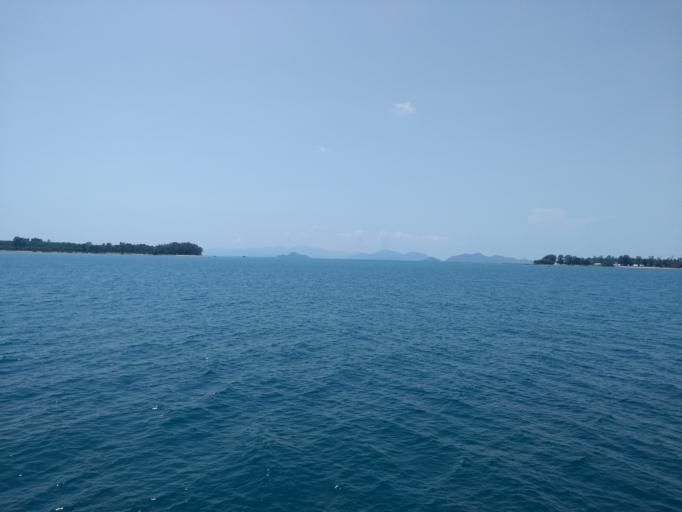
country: TH
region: Trat
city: Ko Kut
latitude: 11.8164
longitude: 102.5242
